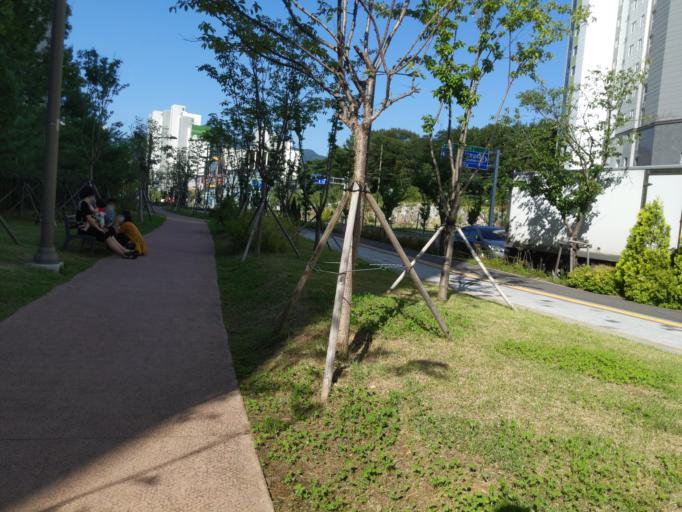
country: KR
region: Daegu
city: Hwawon
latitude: 35.7993
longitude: 128.5312
